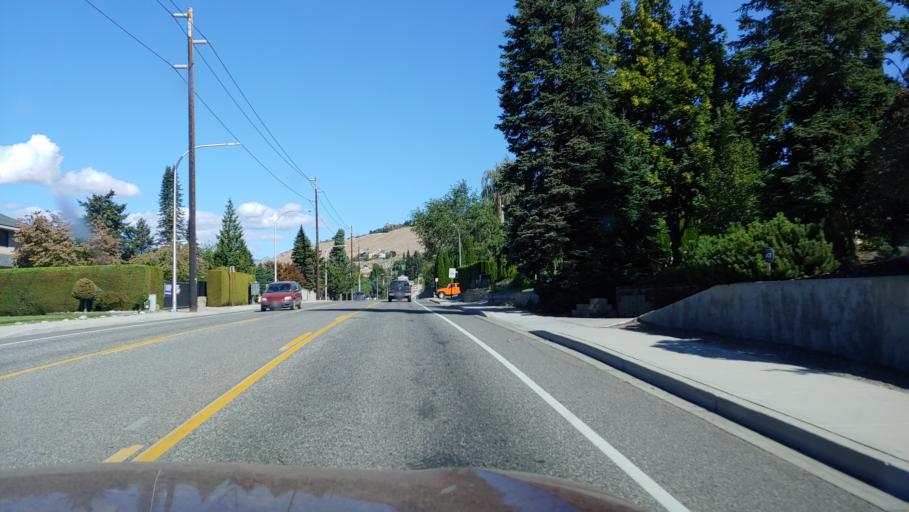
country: US
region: Washington
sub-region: Douglas County
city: East Wenatchee Bench
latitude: 47.4309
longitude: -120.2815
